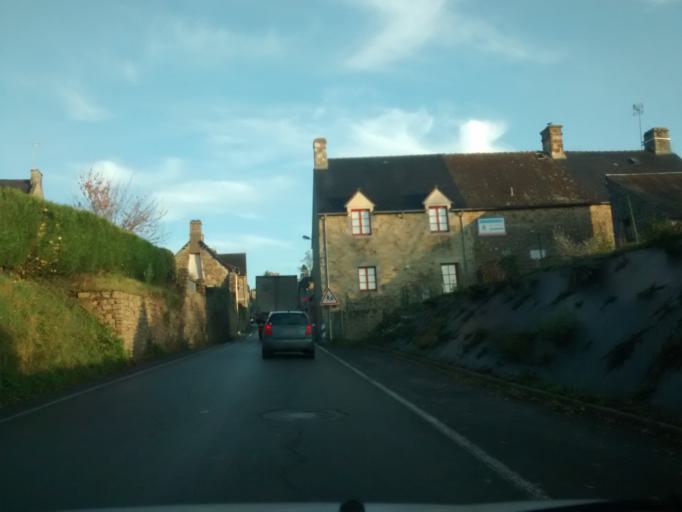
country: FR
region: Brittany
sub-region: Departement d'Ille-et-Vilaine
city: Tremblay
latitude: 48.4208
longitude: -1.4740
